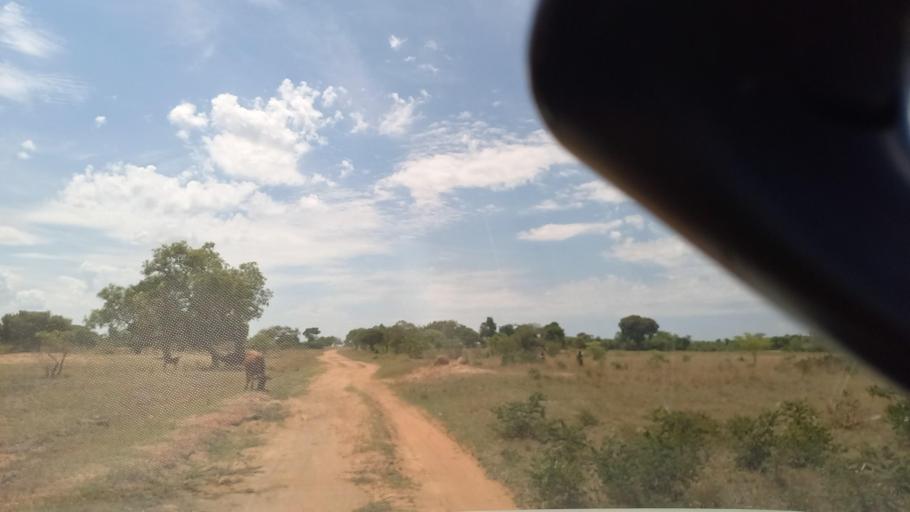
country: ZM
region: Southern
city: Mazabuka
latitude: -16.1484
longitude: 27.7766
